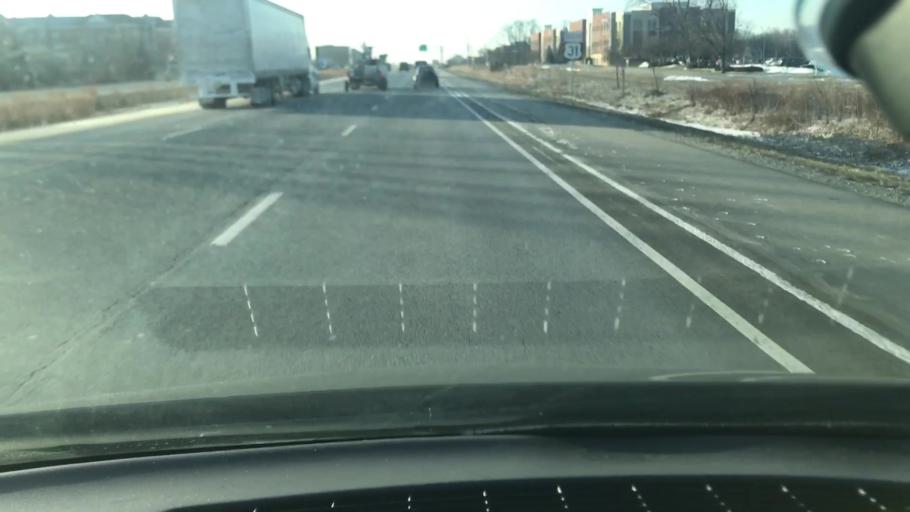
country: US
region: Indiana
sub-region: Hamilton County
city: Carmel
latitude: 39.9699
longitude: -86.1579
